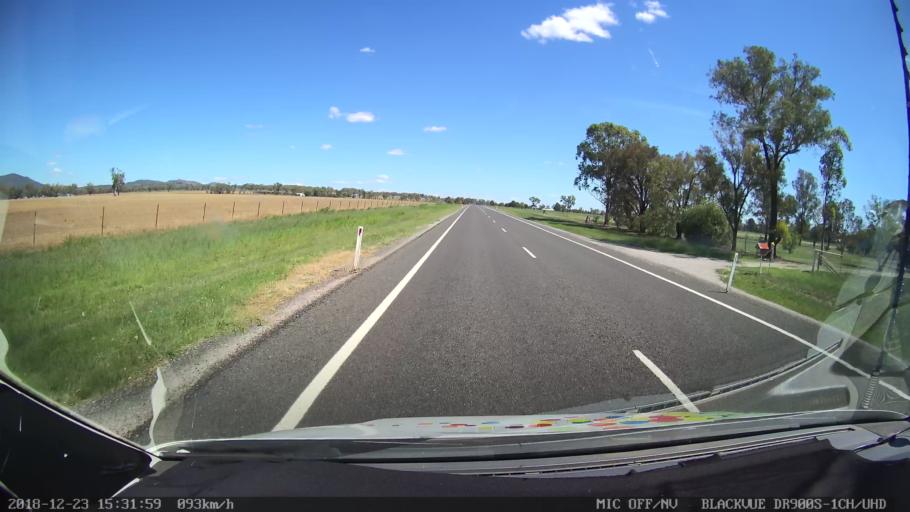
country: AU
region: New South Wales
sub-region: Tamworth Municipality
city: East Tamworth
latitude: -30.9804
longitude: 150.8713
